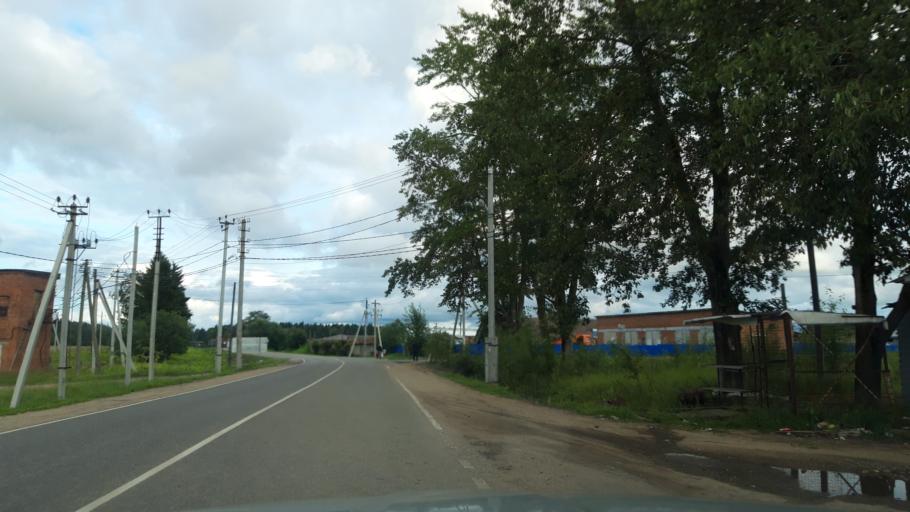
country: RU
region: Moskovskaya
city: Istra
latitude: 56.0939
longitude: 36.8023
